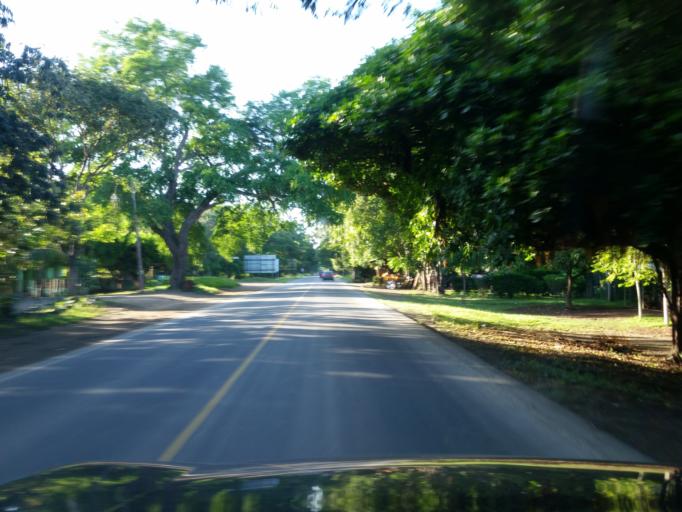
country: NI
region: Rivas
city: Buenos Aires
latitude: 11.4617
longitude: -85.8471
